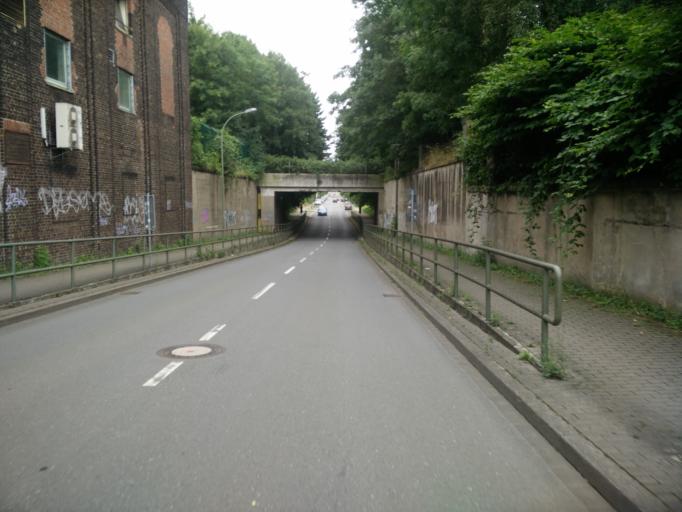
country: DE
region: North Rhine-Westphalia
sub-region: Regierungsbezirk Arnsberg
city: Herne
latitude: 51.5179
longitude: 7.2058
